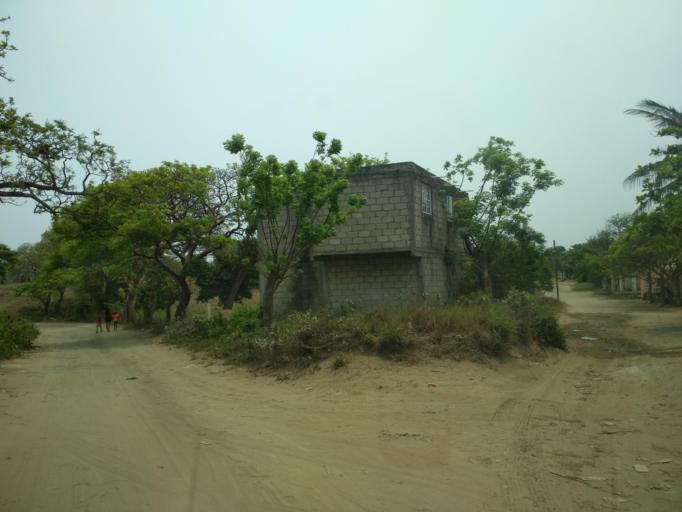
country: MX
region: Veracruz
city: Anton Lizardo
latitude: 19.0603
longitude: -95.9924
